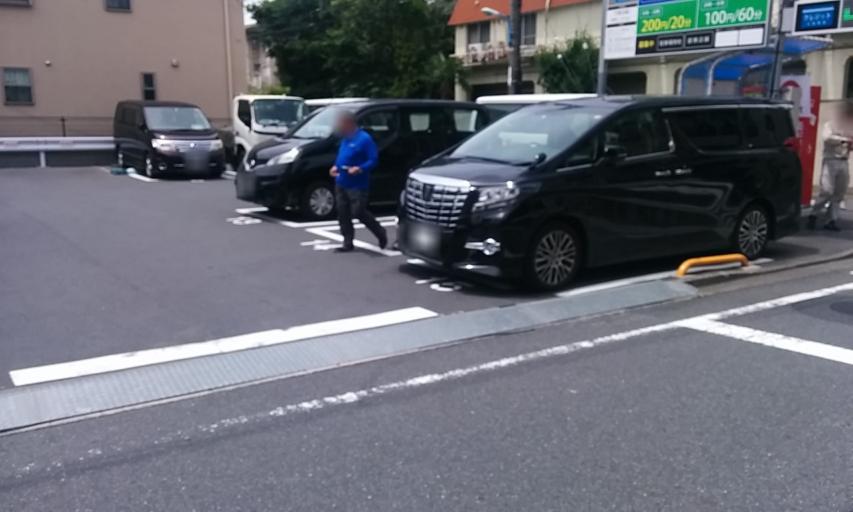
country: JP
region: Tokyo
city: Tokyo
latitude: 35.7206
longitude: 139.7042
